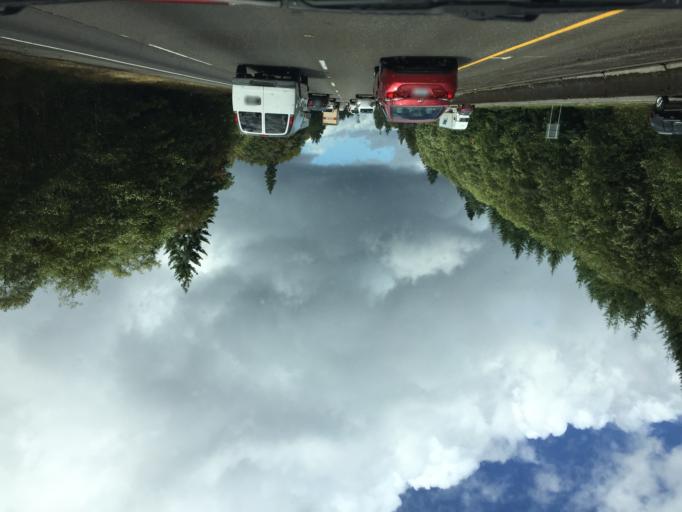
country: US
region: Washington
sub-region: Lewis County
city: Winlock
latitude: 46.4853
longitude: -122.8795
